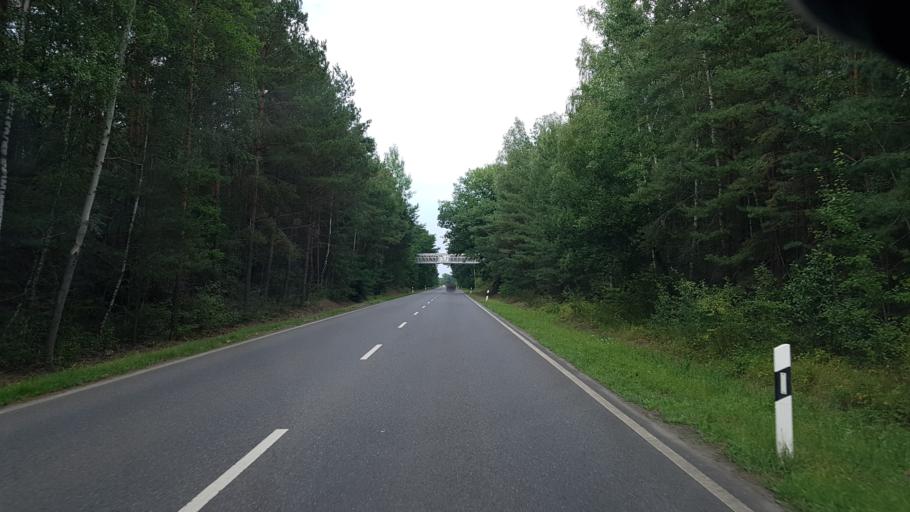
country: DE
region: Brandenburg
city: Lauchhammer
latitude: 51.5016
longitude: 13.7417
